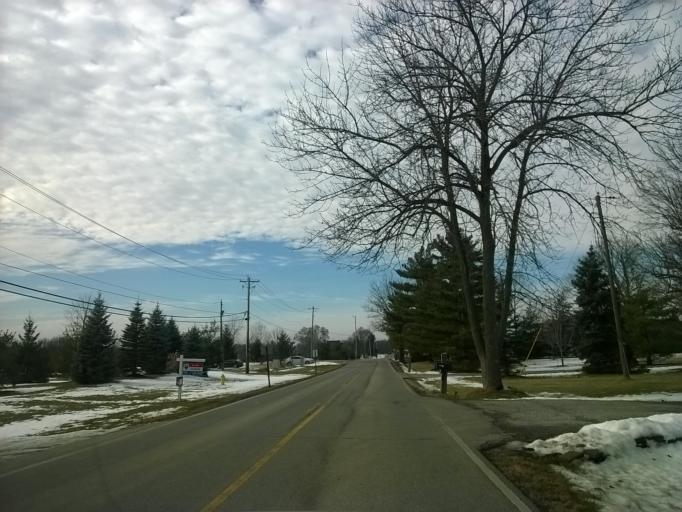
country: US
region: Indiana
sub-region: Boone County
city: Zionsville
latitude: 39.9771
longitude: -86.2341
